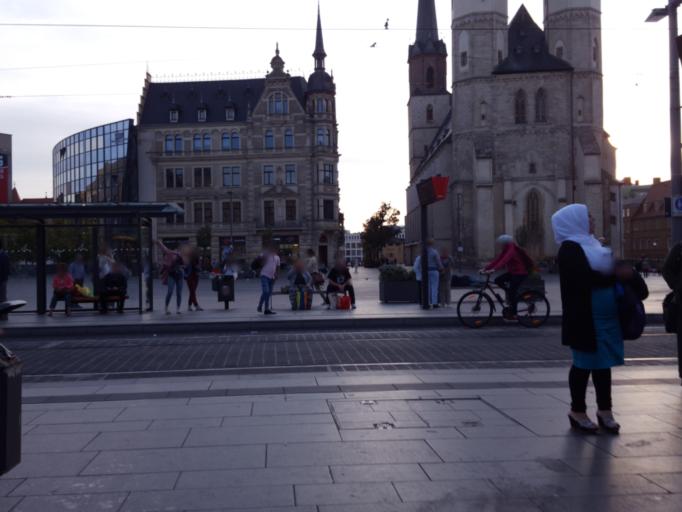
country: DE
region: Saxony-Anhalt
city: Halle (Saale)
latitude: 51.4827
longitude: 11.9701
